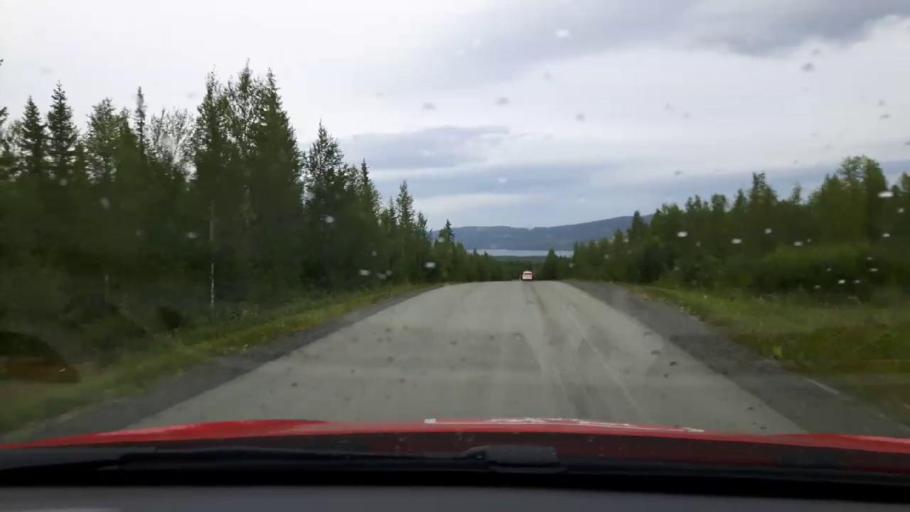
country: SE
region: Jaemtland
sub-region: Are Kommun
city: Are
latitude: 63.4310
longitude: 13.2139
